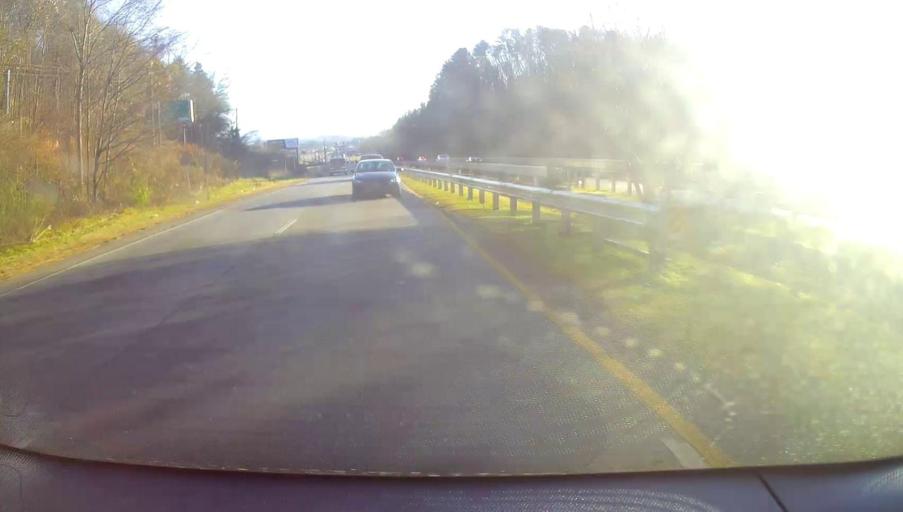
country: US
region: Alabama
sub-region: Calhoun County
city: Oxford
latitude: 33.6211
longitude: -85.8280
